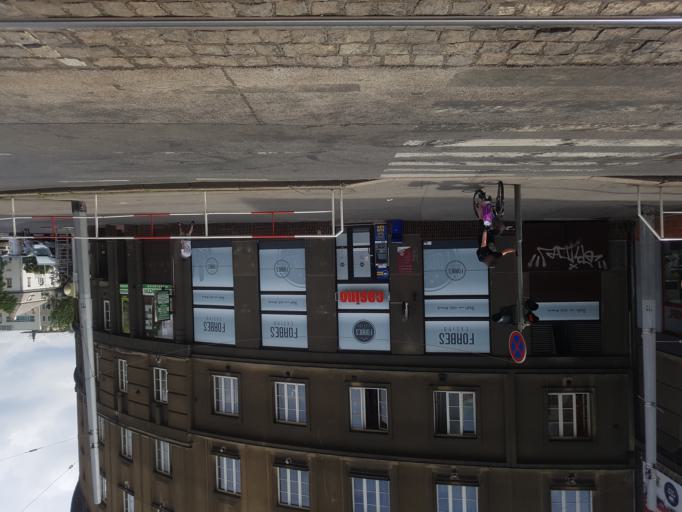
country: CZ
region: Praha
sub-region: Praha 8
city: Liben
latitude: 50.0900
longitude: 14.4681
